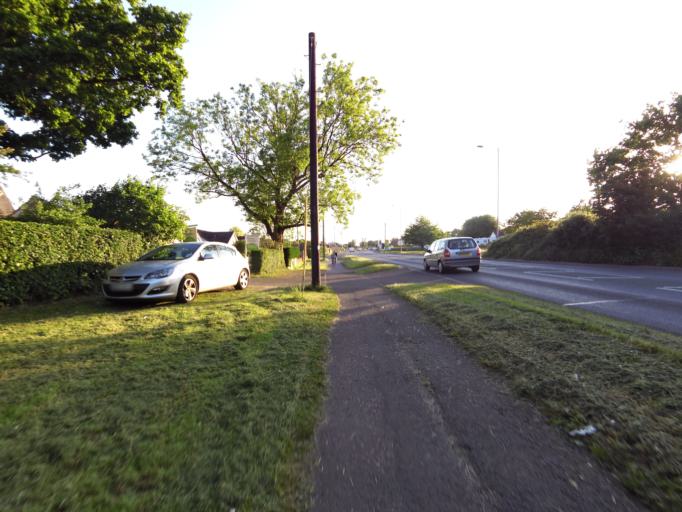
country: GB
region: England
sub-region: Suffolk
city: Kesgrave
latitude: 52.0644
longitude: 1.2193
